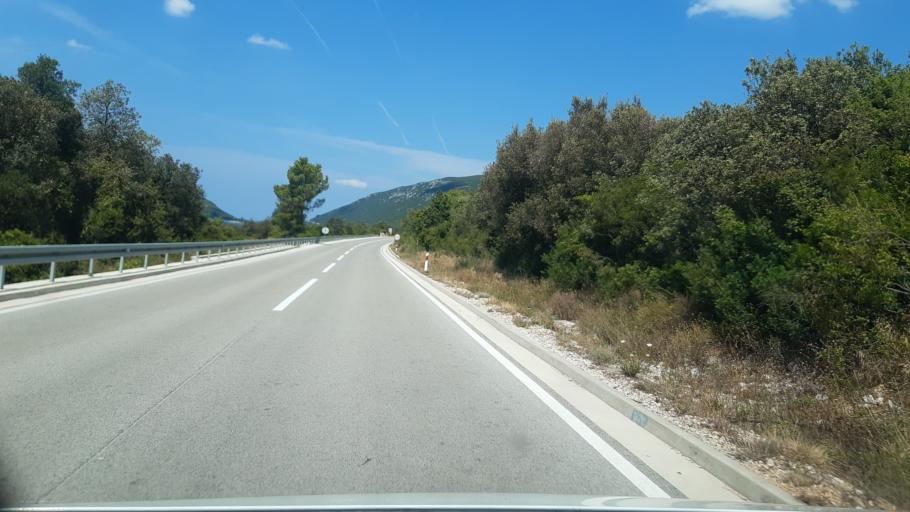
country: HR
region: Dubrovacko-Neretvanska
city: Ston
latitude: 42.8571
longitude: 17.7088
